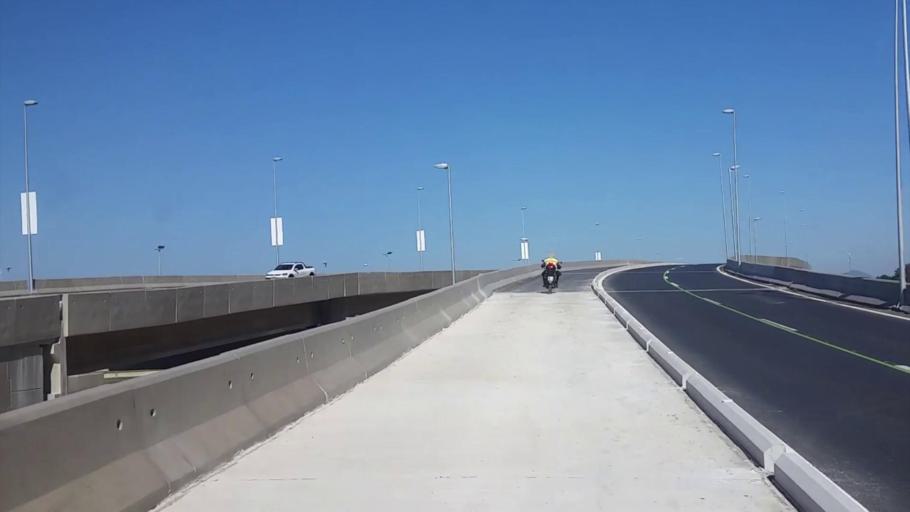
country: BR
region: Rio de Janeiro
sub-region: Nilopolis
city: Nilopolis
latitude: -22.9717
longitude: -43.4016
